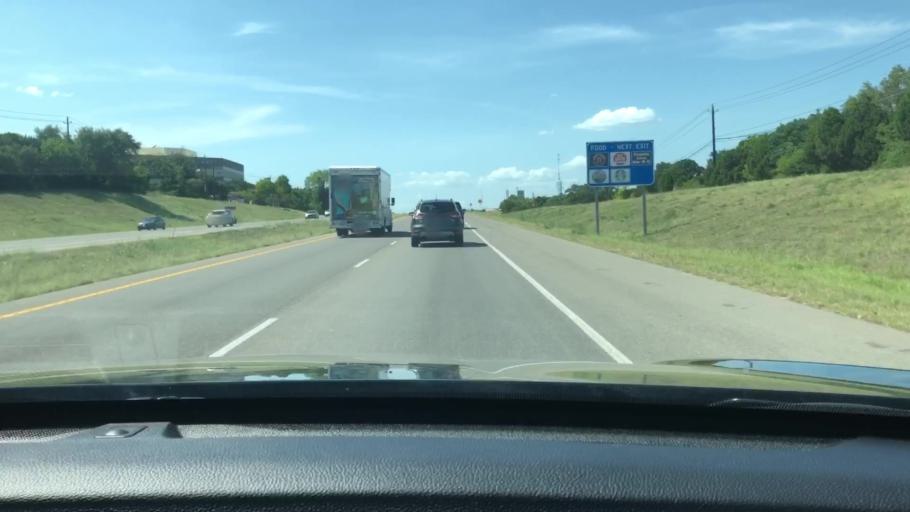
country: US
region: Texas
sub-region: Travis County
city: Lost Creek
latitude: 30.2841
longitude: -97.8243
